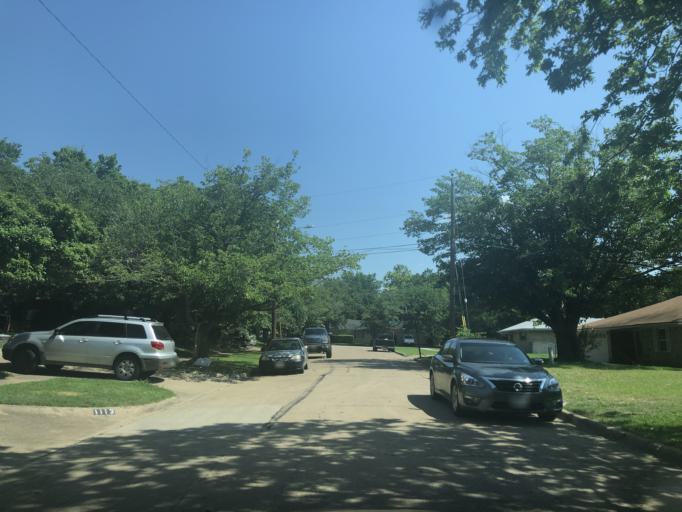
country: US
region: Texas
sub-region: Dallas County
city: Grand Prairie
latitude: 32.7311
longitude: -97.0024
